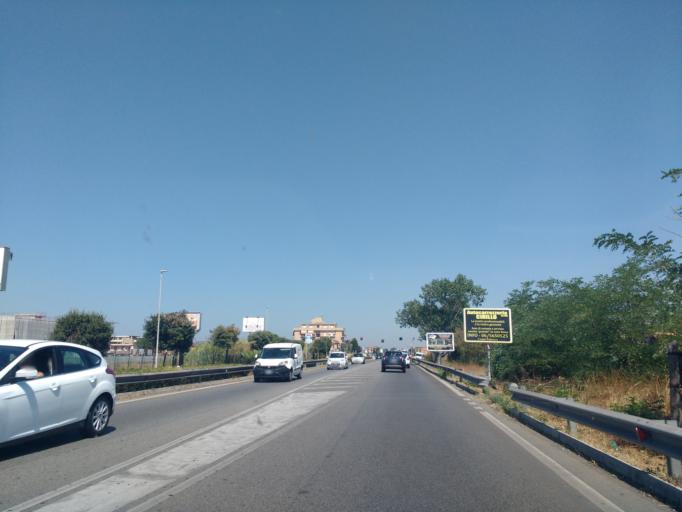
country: IT
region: Latium
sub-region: Citta metropolitana di Roma Capitale
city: Lido di Ostia
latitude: 41.7610
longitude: 12.2687
